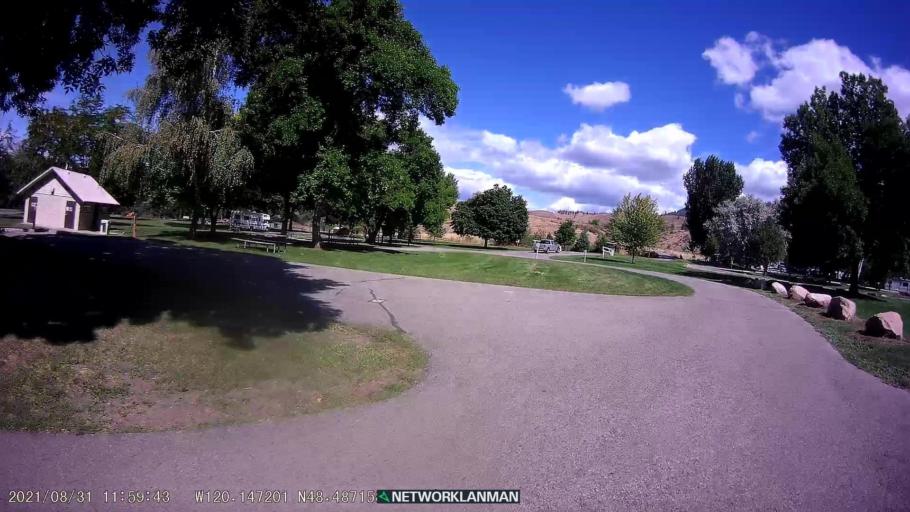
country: US
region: Washington
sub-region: Okanogan County
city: Brewster
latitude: 48.4867
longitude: -120.1463
